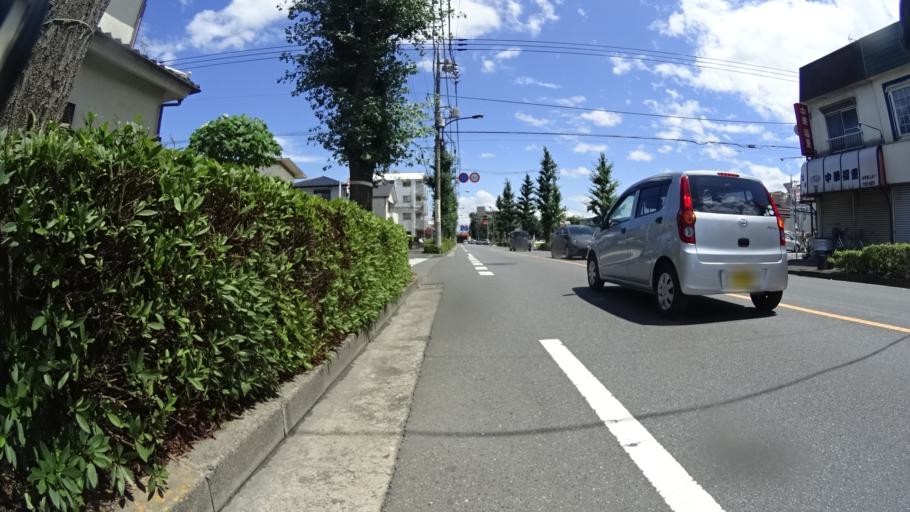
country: JP
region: Tokyo
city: Ome
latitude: 35.7793
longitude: 139.2903
